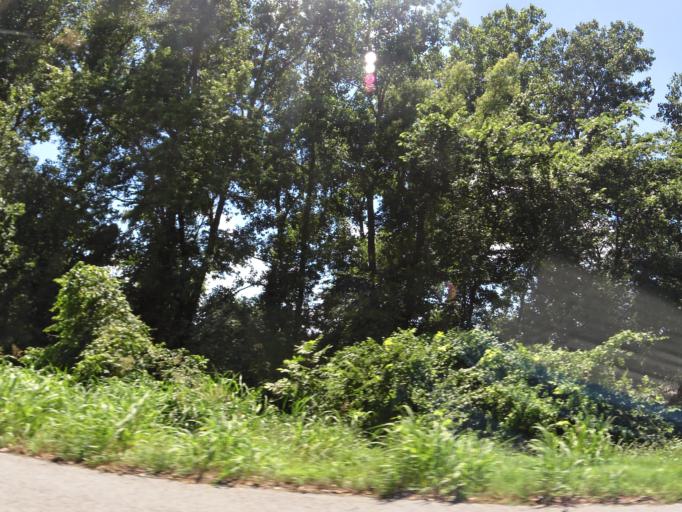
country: US
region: Missouri
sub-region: Pemiscot County
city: Caruthersville
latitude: 36.1269
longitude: -89.6201
